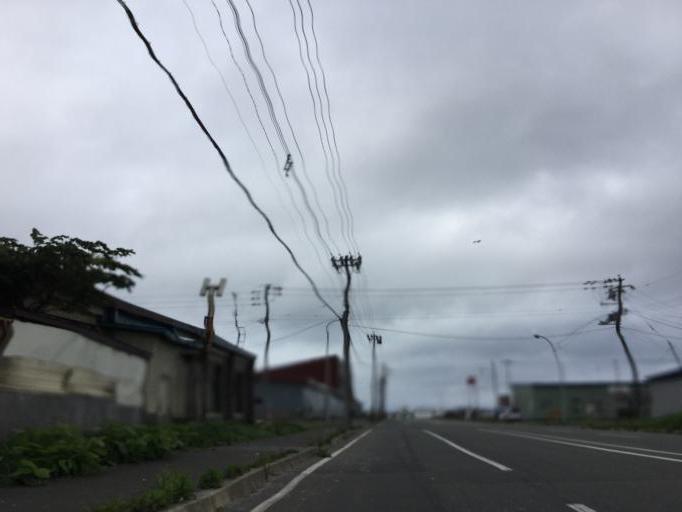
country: JP
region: Hokkaido
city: Wakkanai
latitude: 45.4075
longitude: 141.6822
